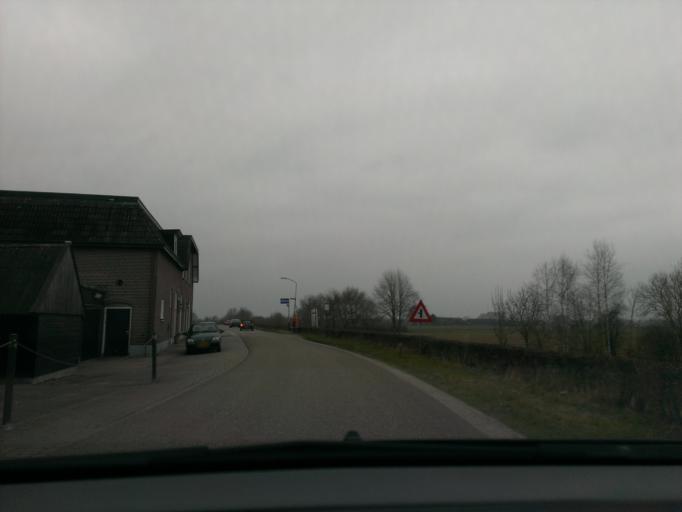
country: NL
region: Overijssel
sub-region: Gemeente Olst-Wijhe
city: Wijhe
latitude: 52.3939
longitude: 6.1229
